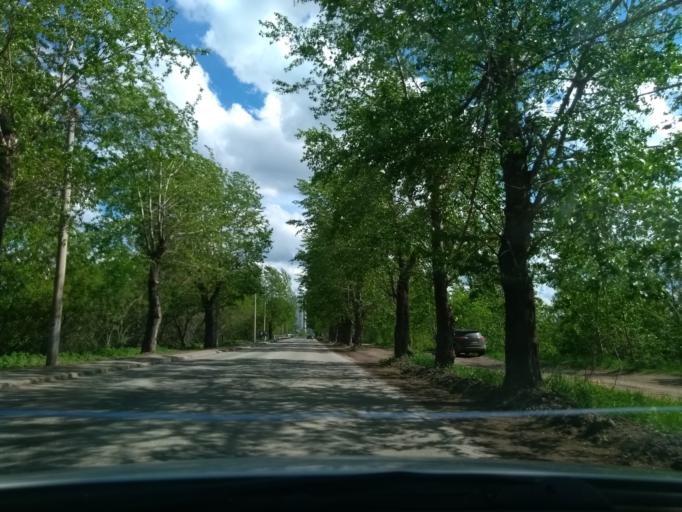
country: RU
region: Perm
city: Kondratovo
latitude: 58.0033
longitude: 56.1281
